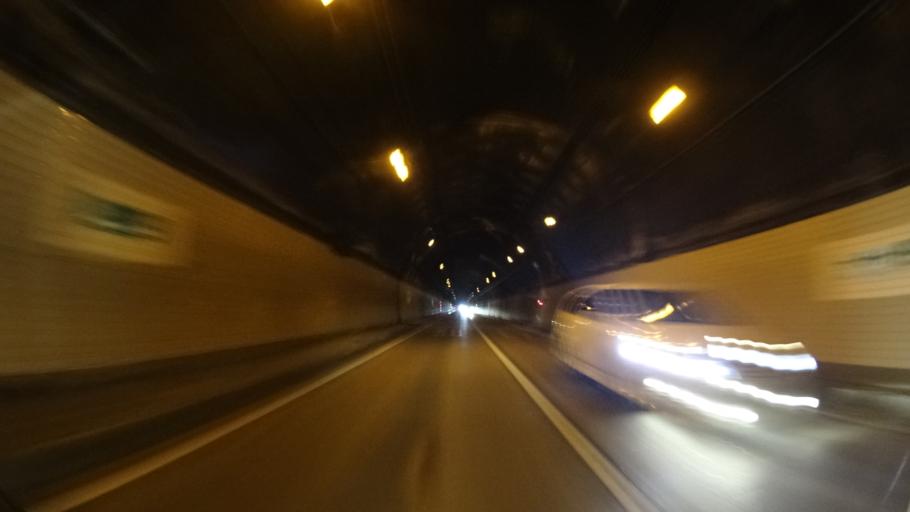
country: JP
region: Ehime
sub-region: Nishiuwa-gun
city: Ikata-cho
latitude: 33.4963
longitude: 132.3786
